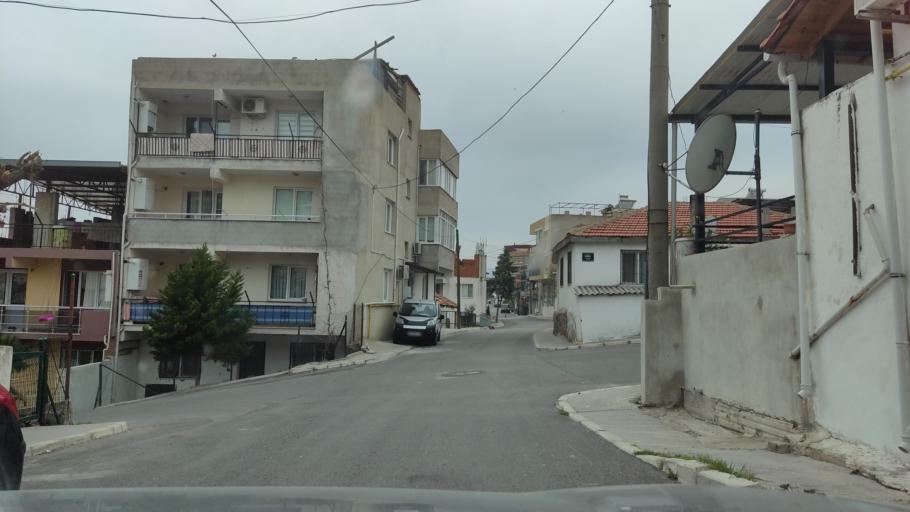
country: TR
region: Izmir
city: Karsiyaka
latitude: 38.5013
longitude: 27.0776
